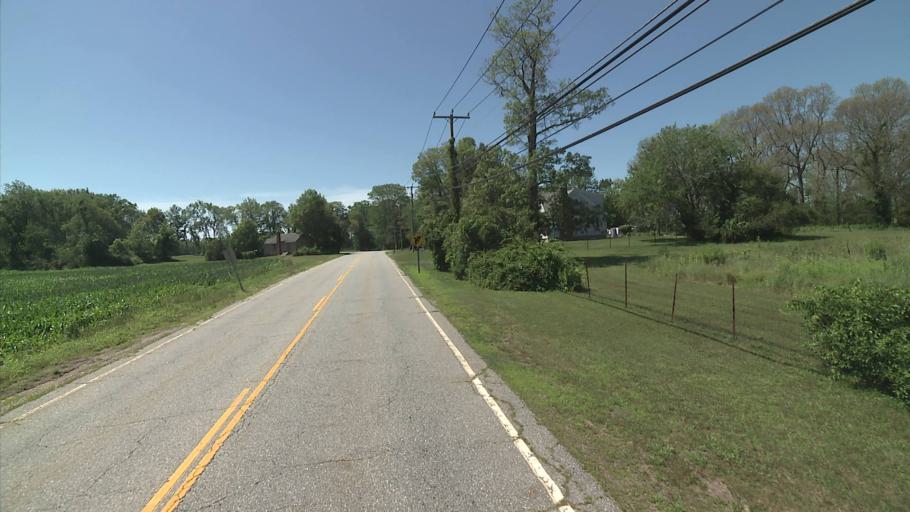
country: US
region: Connecticut
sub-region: New London County
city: Colchester
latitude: 41.6097
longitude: -72.2749
